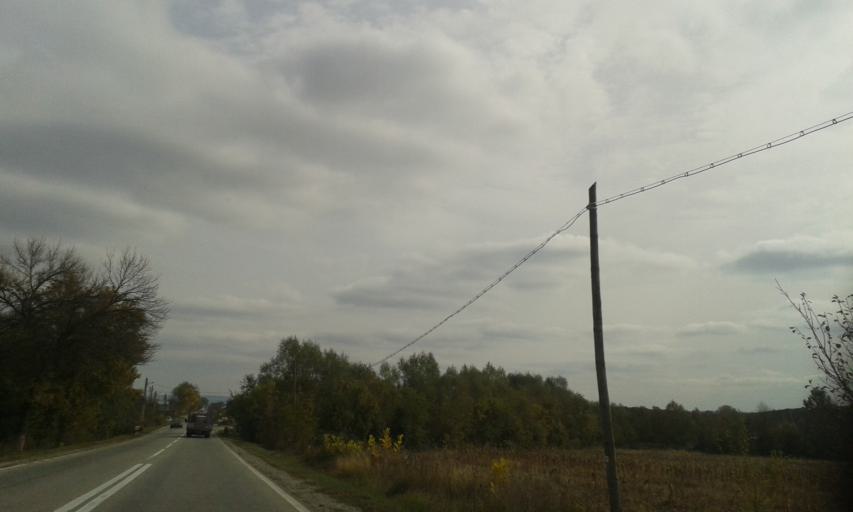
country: RO
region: Gorj
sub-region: Comuna Scoarta
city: Scoarta
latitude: 45.0308
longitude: 23.4174
